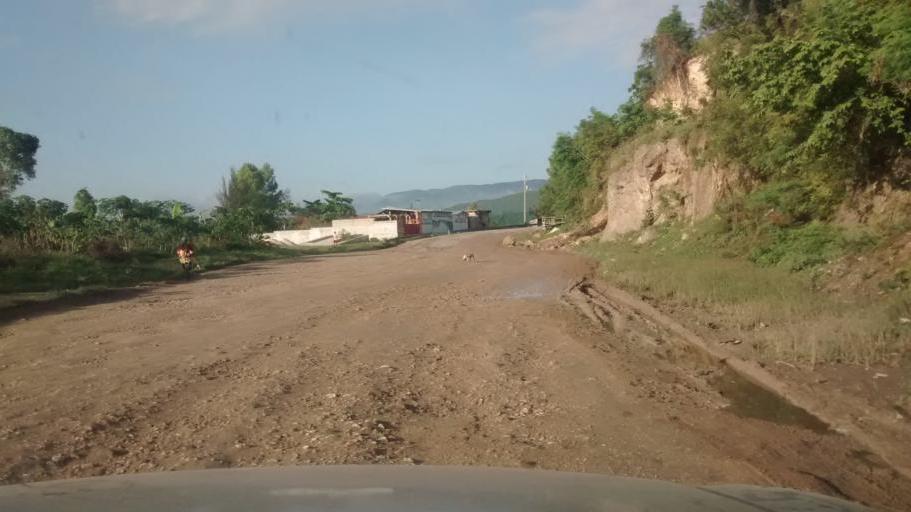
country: HT
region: Nippes
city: Miragoane
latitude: 18.4263
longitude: -73.0501
